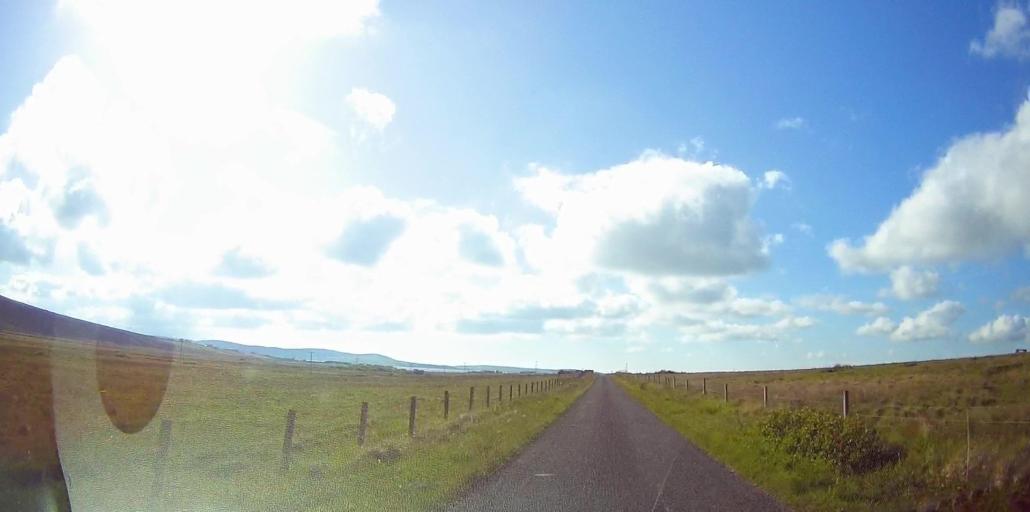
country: GB
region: Scotland
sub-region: Orkney Islands
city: Stromness
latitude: 58.9814
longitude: -3.1800
